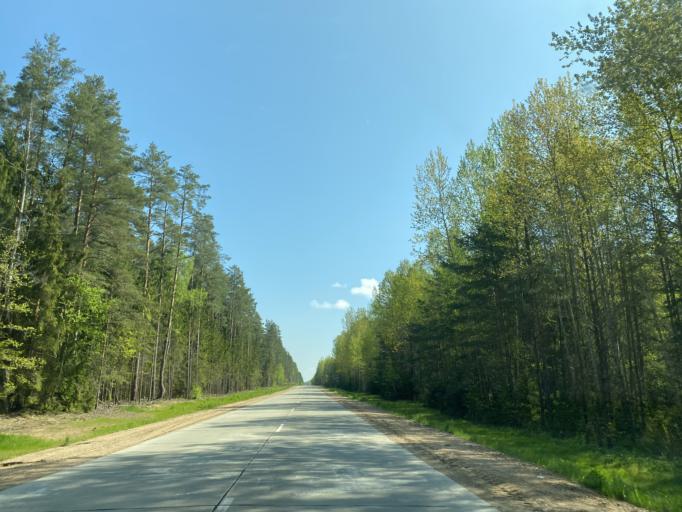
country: BY
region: Minsk
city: Horad Barysaw
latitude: 54.1697
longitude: 28.5158
